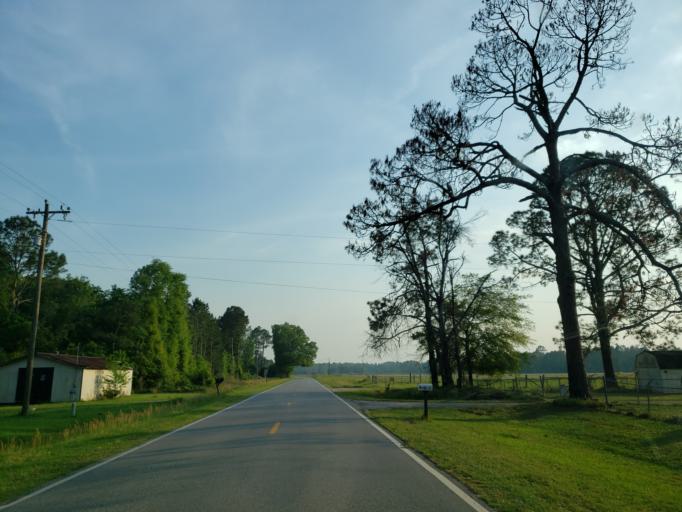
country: US
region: Georgia
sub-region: Cook County
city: Sparks
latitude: 31.1998
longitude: -83.4243
